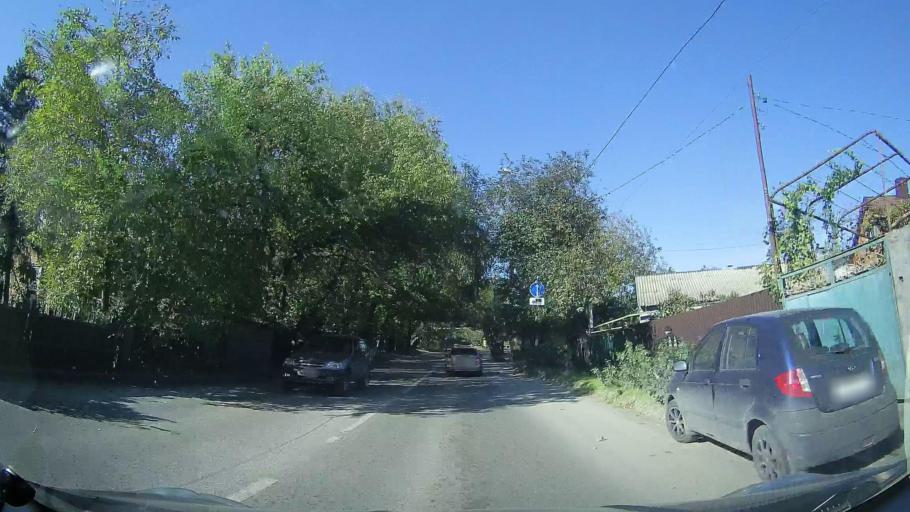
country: RU
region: Rostov
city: Rostov-na-Donu
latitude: 47.2271
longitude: 39.6725
